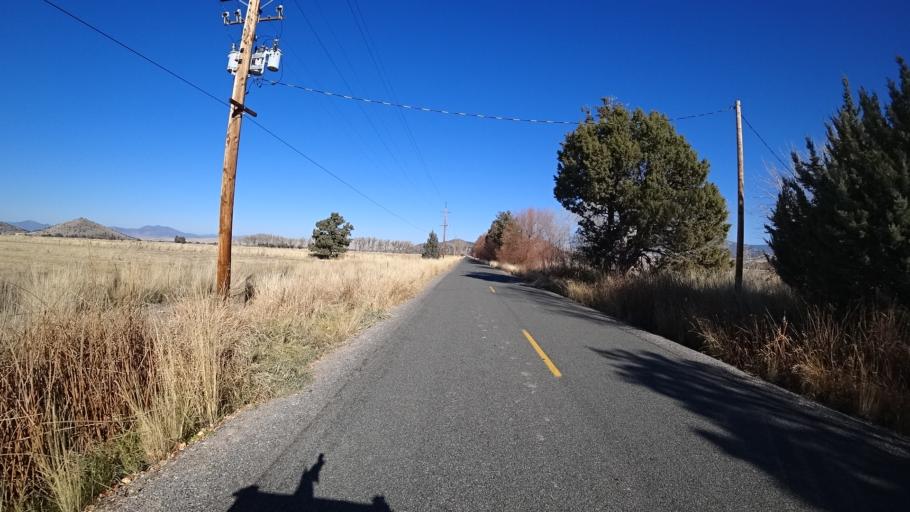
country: US
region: California
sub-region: Siskiyou County
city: Montague
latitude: 41.6772
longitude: -122.3698
